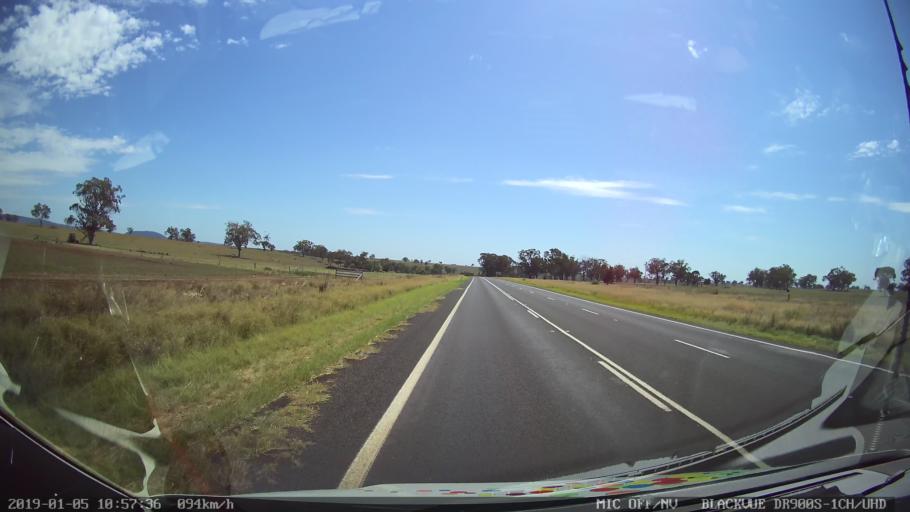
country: AU
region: New South Wales
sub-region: Warrumbungle Shire
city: Coonabarabran
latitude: -31.4299
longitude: 149.1719
